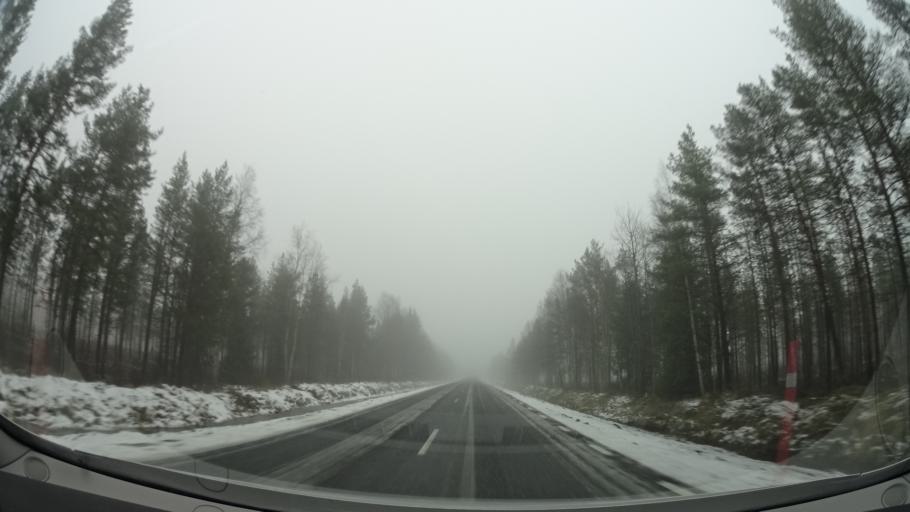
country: SE
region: Vaesterbotten
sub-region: Asele Kommun
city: Insjon
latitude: 64.2894
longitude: 17.6487
